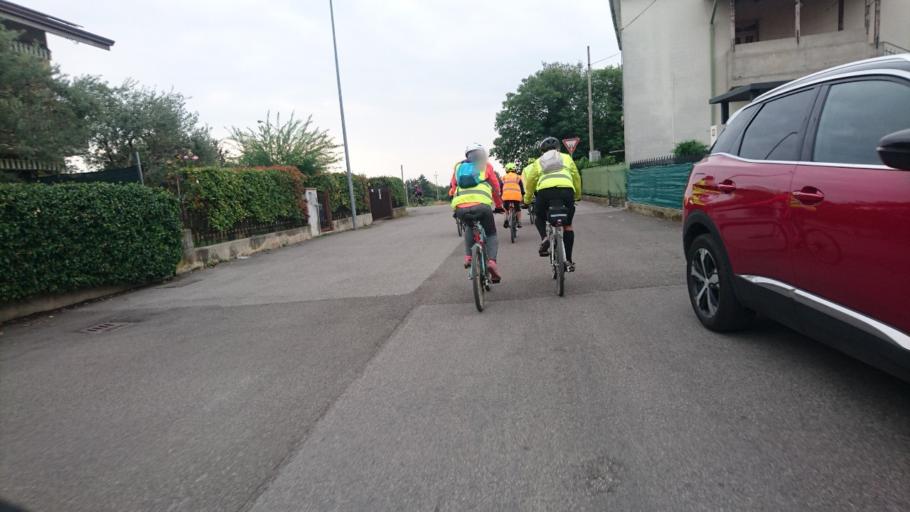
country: IT
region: Veneto
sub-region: Provincia di Verona
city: San Giovanni Lupatoto
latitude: 45.4231
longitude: 11.0466
